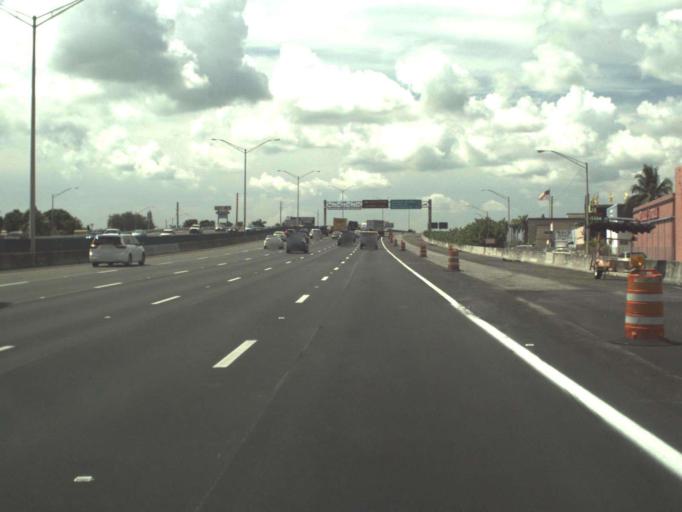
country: US
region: Florida
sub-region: Broward County
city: Pembroke Park
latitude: 26.0003
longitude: -80.1668
